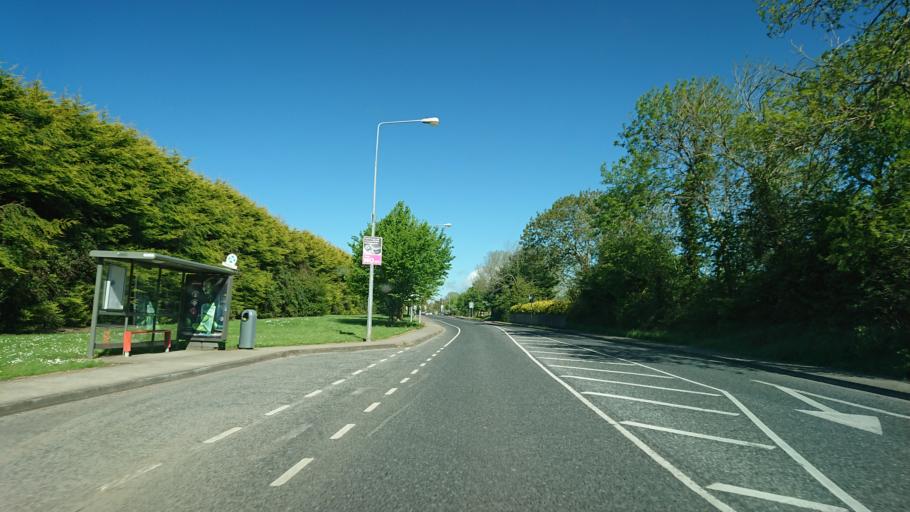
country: IE
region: Munster
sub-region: Waterford
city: Waterford
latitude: 52.2366
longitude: -7.0603
